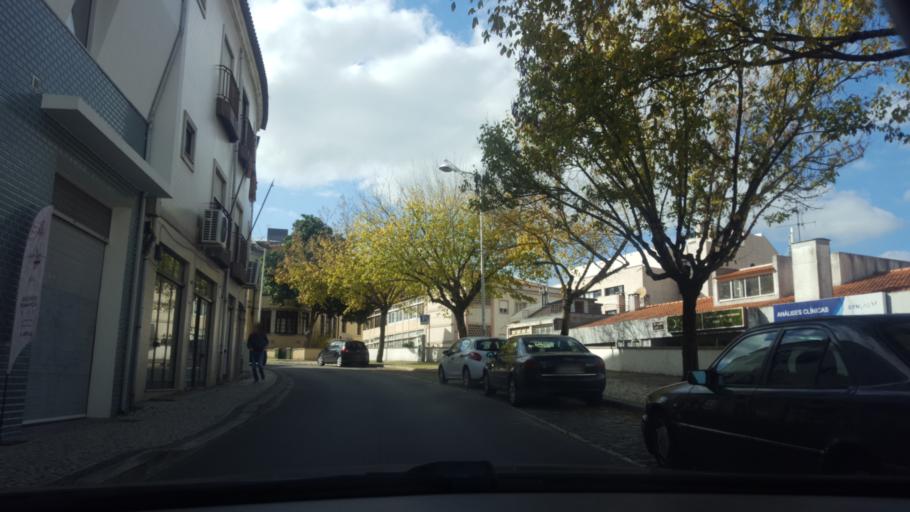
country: PT
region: Leiria
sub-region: Leiria
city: Leiria
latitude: 39.7426
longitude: -8.8084
